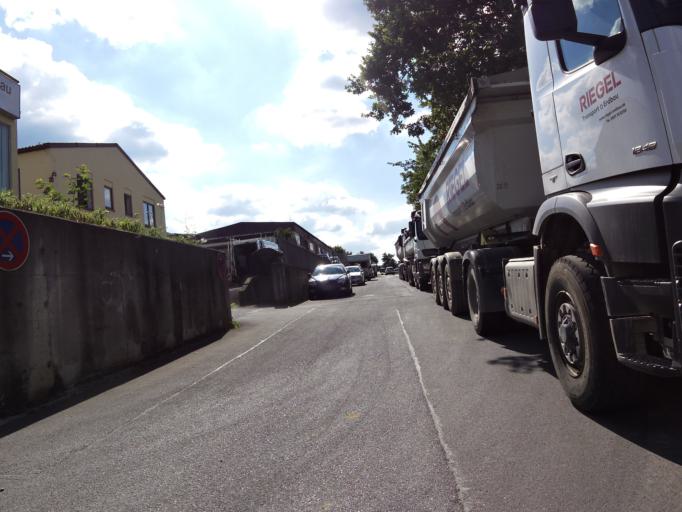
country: DE
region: Bavaria
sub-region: Regierungsbezirk Unterfranken
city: Gerbrunn
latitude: 49.7880
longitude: 9.9874
